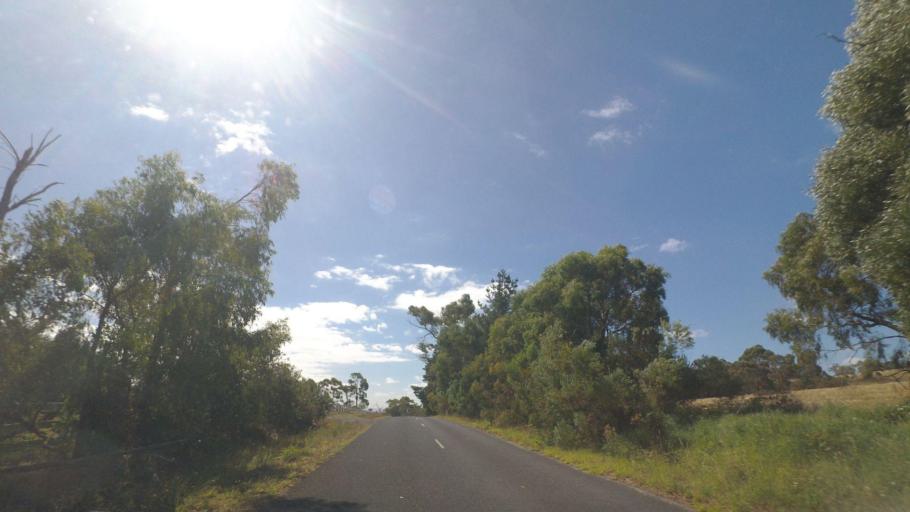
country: AU
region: Victoria
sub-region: Cardinia
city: Koo-Wee-Rup
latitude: -38.2889
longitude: 145.6657
